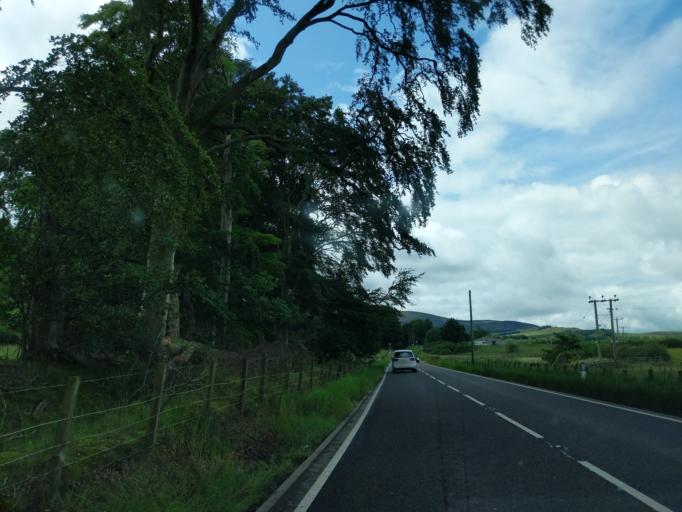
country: GB
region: Scotland
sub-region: South Lanarkshire
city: Biggar
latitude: 55.6050
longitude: -3.5895
